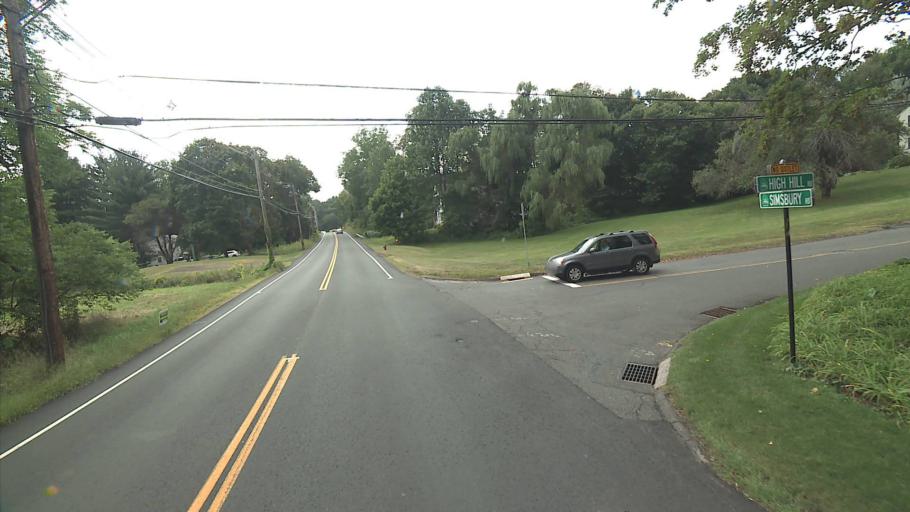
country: US
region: Connecticut
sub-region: Hartford County
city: West Hartford
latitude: 41.8186
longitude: -72.7675
